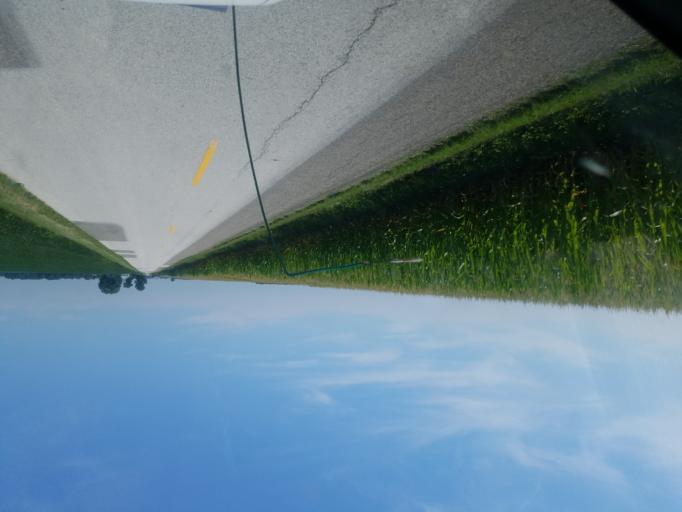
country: US
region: Ohio
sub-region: Shelby County
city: Jackson Center
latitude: 40.5366
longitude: -84.0120
